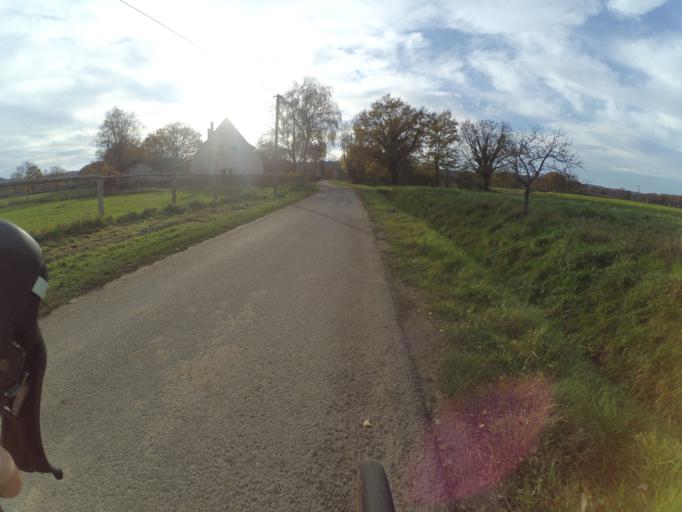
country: DE
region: North Rhine-Westphalia
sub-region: Regierungsbezirk Munster
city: Tecklenburg
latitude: 52.2401
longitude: 7.8029
